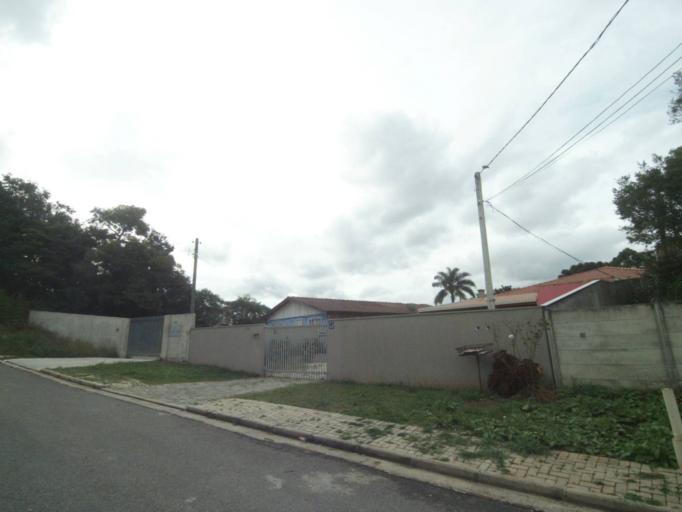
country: BR
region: Parana
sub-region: Curitiba
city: Curitiba
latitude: -25.4403
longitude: -49.3117
